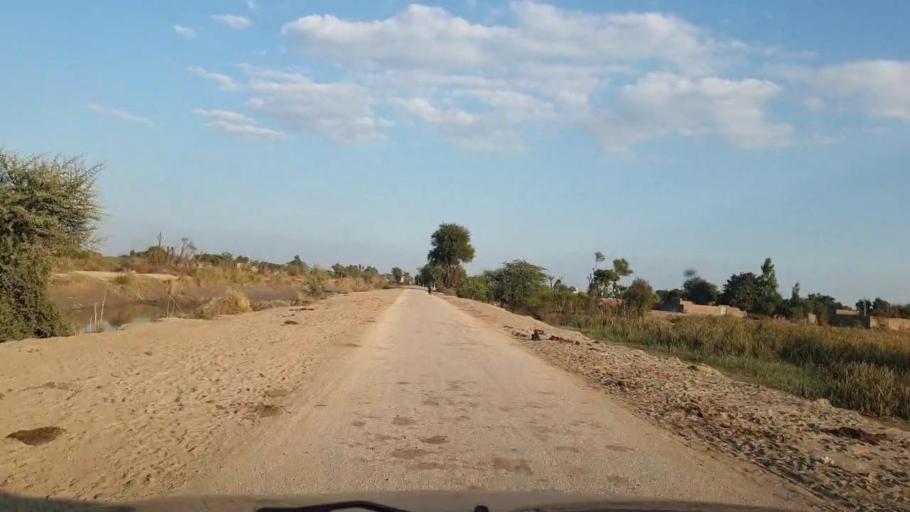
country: PK
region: Sindh
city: Sinjhoro
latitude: 25.9932
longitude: 68.7658
